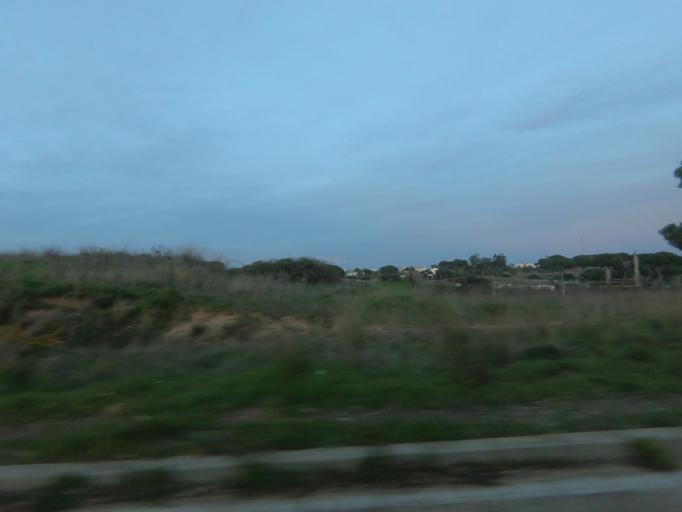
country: PT
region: Setubal
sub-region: Setubal
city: Setubal
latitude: 38.5165
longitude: -8.8595
